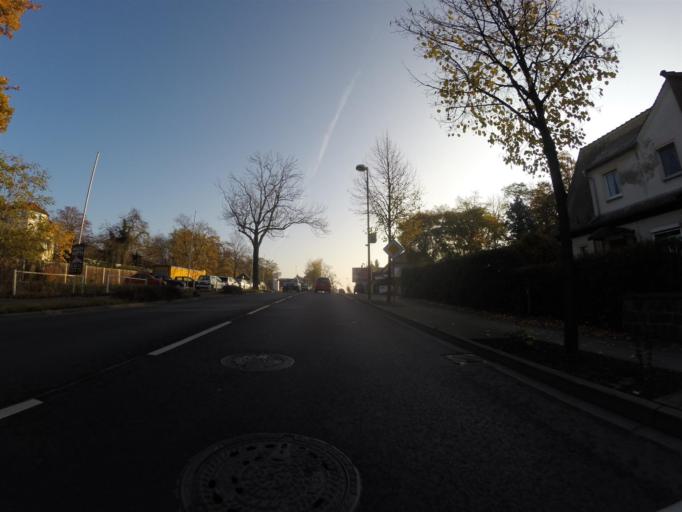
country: DE
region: Saxony
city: Markranstadt
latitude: 51.3469
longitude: 12.2547
